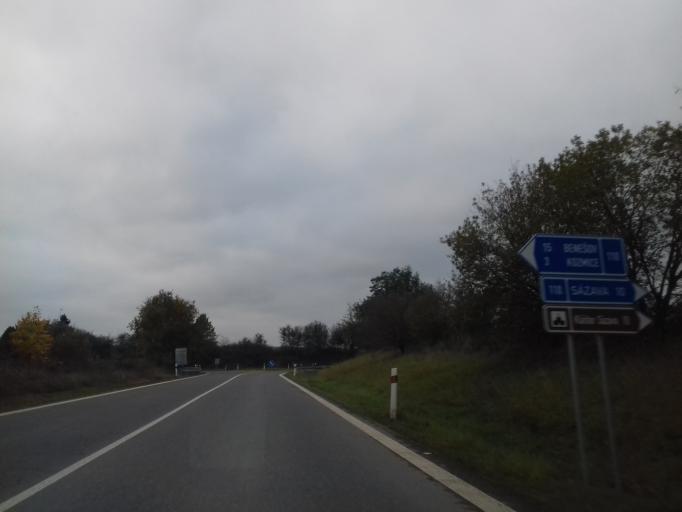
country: CZ
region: Central Bohemia
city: Divisov
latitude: 49.8381
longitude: 14.8264
